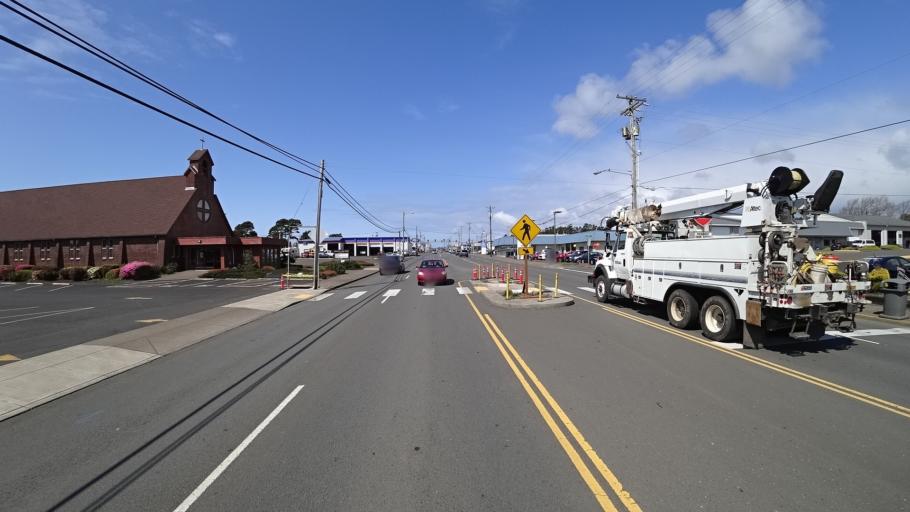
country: US
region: Oregon
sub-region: Lincoln County
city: Newport
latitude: 44.6430
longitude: -124.0531
